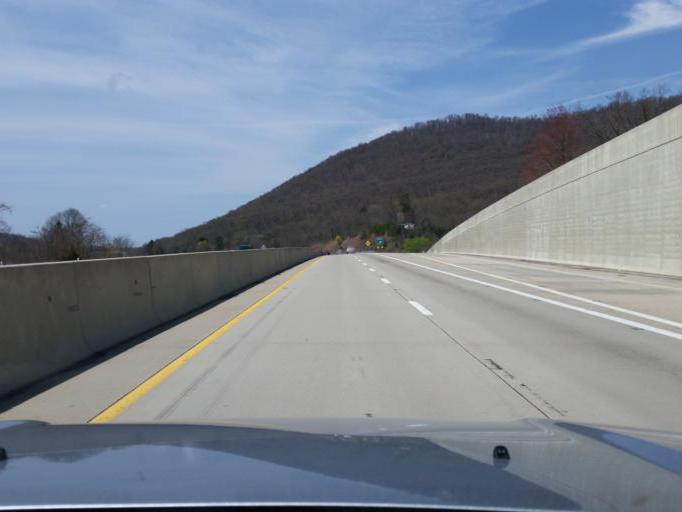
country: US
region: Pennsylvania
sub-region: Perry County
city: Duncannon
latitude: 40.3767
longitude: -77.0022
